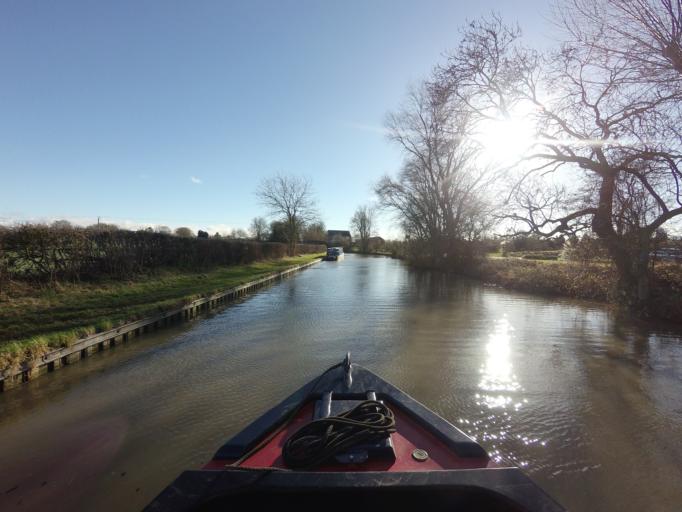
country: GB
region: England
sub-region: Northamptonshire
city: Bugbrooke
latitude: 52.2116
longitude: -1.0228
